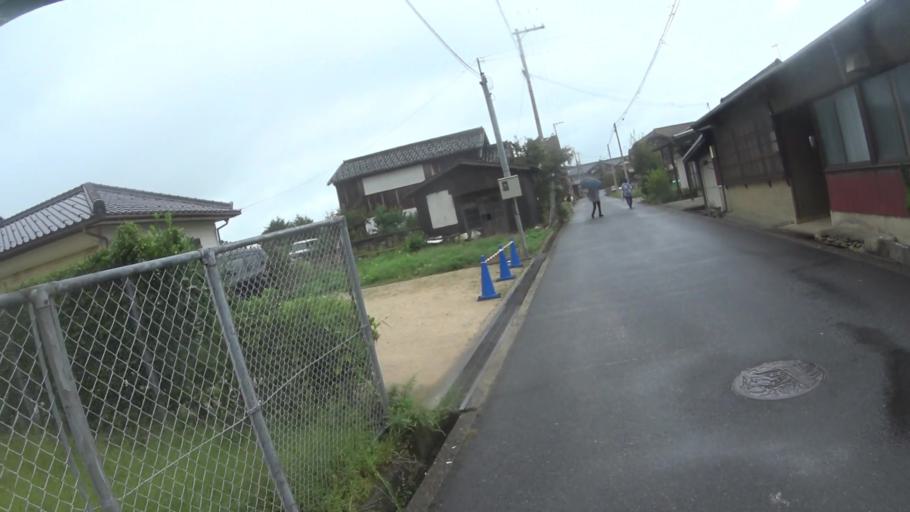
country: JP
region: Hyogo
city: Toyooka
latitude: 35.6589
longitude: 134.9677
